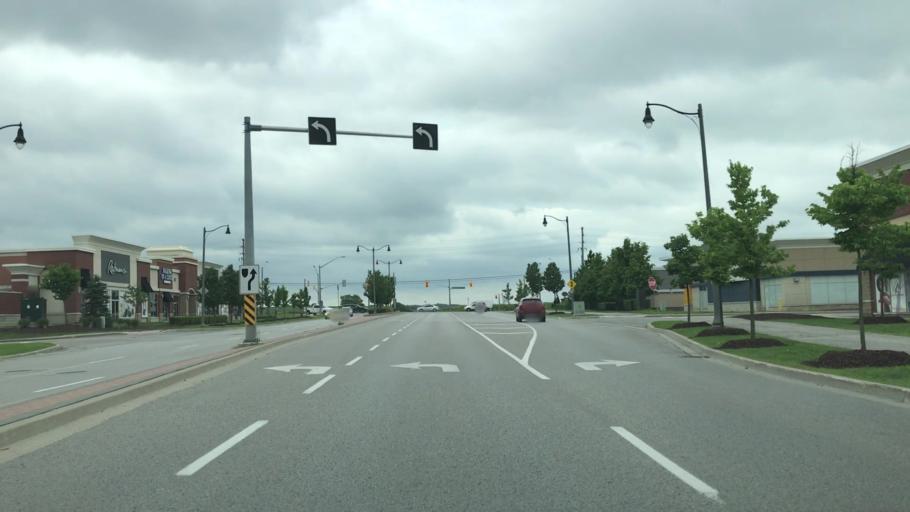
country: CA
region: Ontario
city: Newmarket
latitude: 44.0135
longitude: -79.4152
